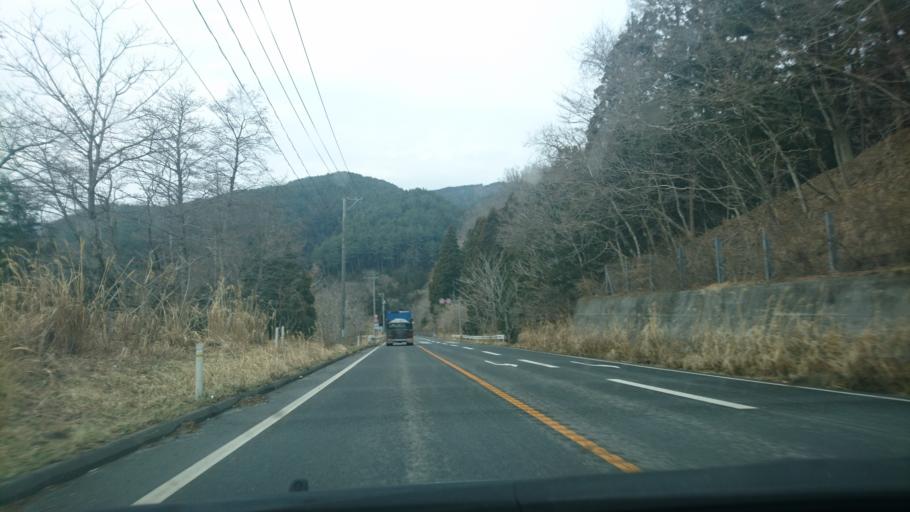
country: JP
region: Iwate
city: Ofunato
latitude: 39.0262
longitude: 141.6838
